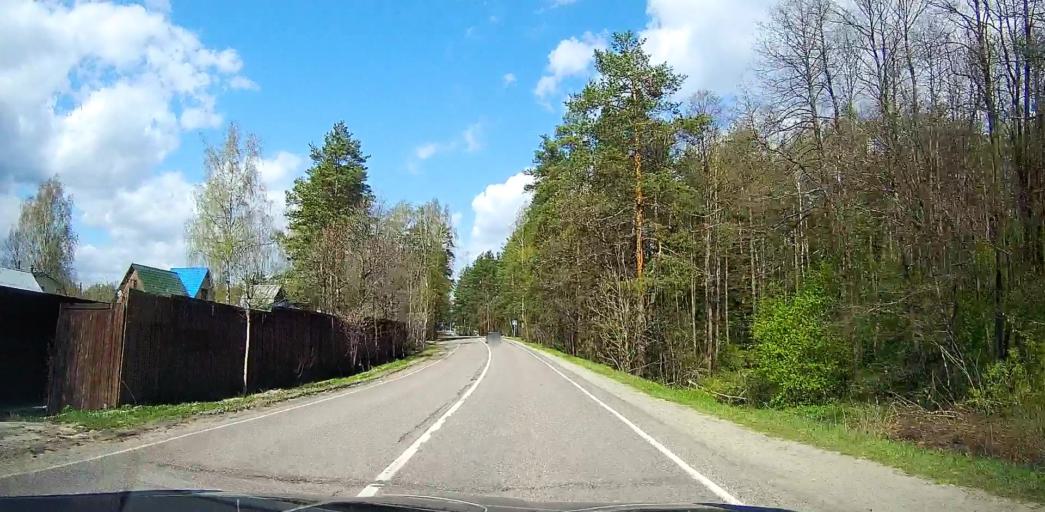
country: RU
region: Moskovskaya
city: Davydovo
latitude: 55.5698
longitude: 38.8231
